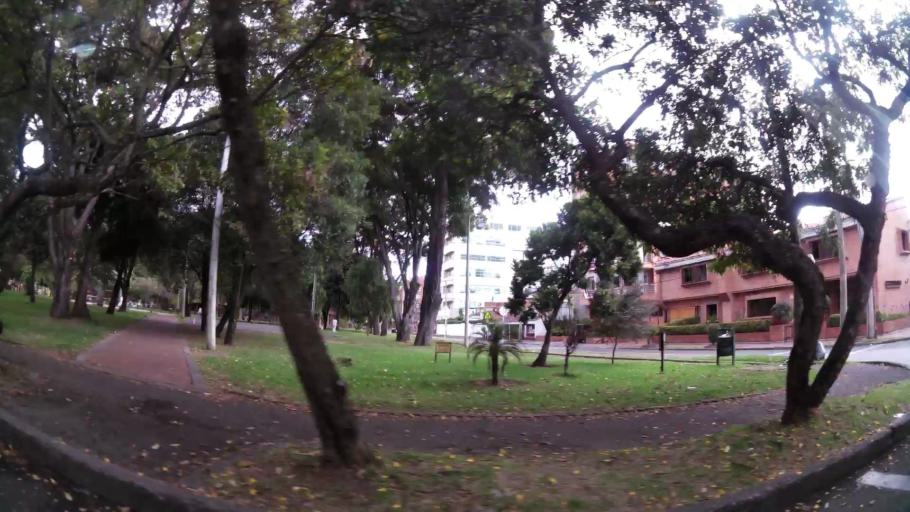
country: CO
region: Bogota D.C.
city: Barrio San Luis
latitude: 4.6914
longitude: -74.0501
